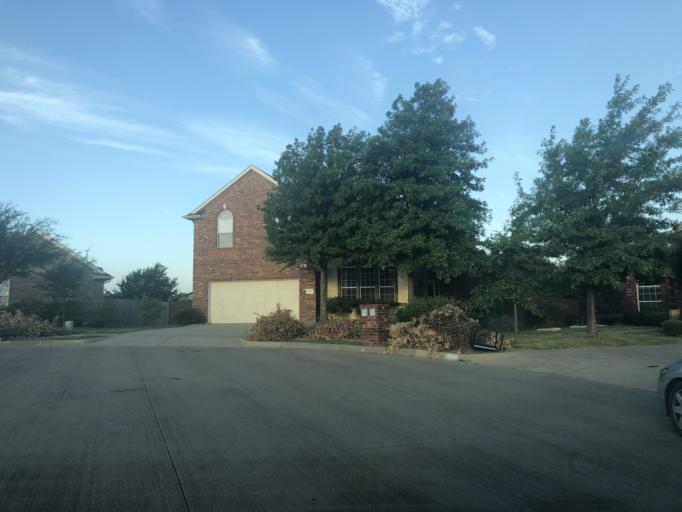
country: US
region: Texas
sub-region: Dallas County
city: Duncanville
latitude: 32.6529
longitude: -96.9684
